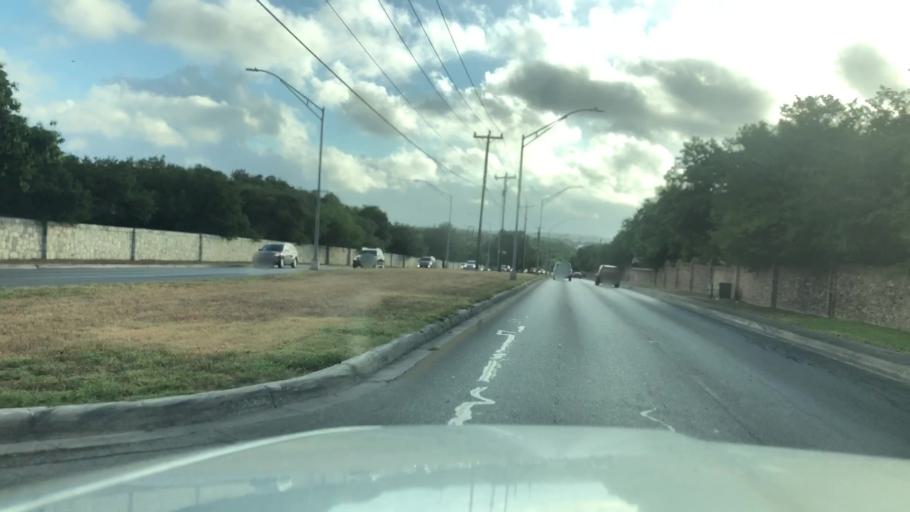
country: US
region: Texas
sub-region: Bexar County
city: Shavano Park
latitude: 29.5672
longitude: -98.5552
